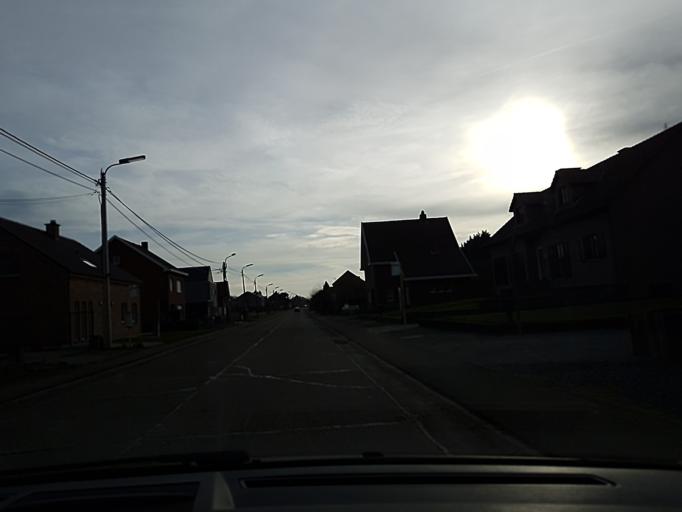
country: BE
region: Flanders
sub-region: Provincie Vlaams-Brabant
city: Rotselaar
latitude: 50.9526
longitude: 4.6759
